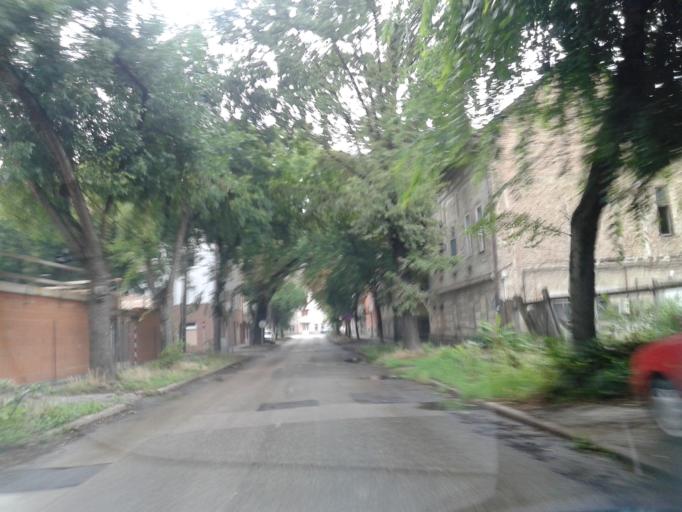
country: HU
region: Csongrad
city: Szeged
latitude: 46.2582
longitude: 20.1615
